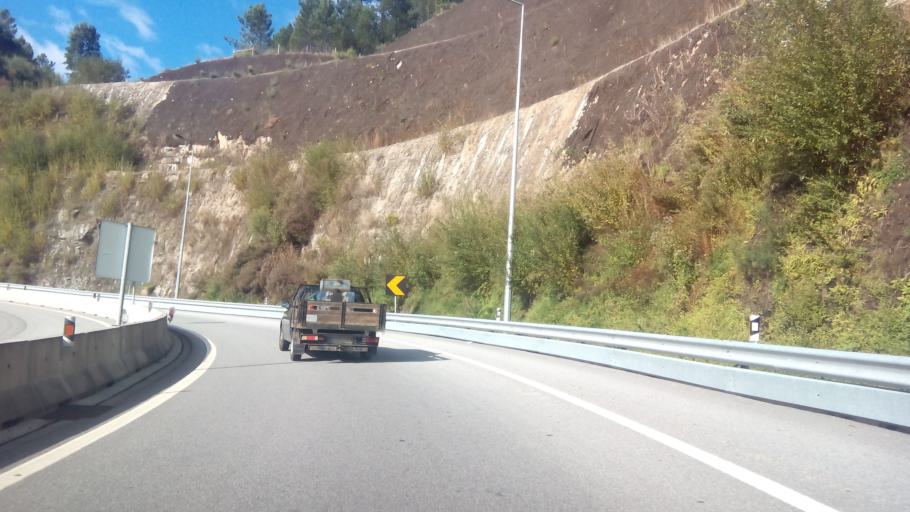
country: PT
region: Porto
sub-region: Amarante
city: Amarante
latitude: 41.2563
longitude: -8.0464
